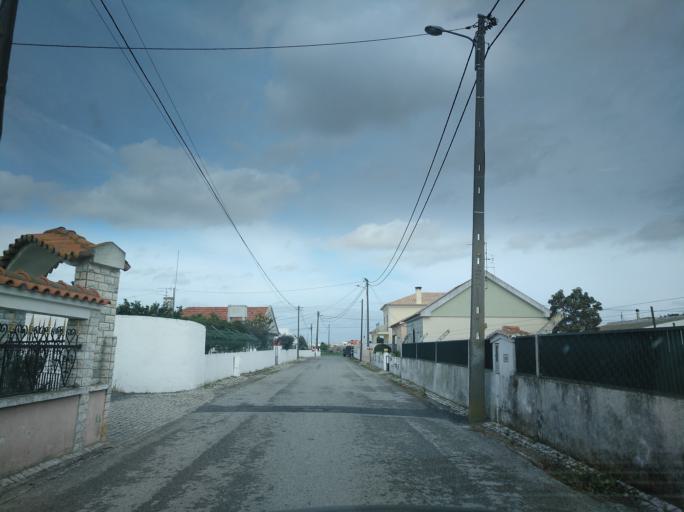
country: PT
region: Setubal
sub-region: Palmela
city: Pinhal Novo
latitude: 38.6745
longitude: -8.9197
